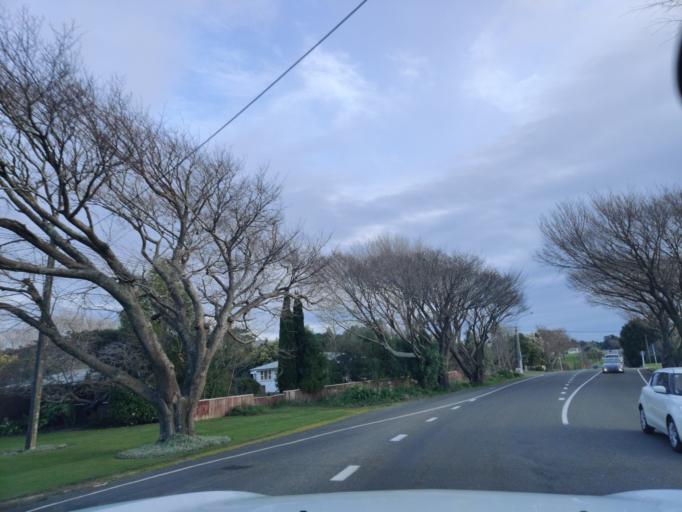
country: NZ
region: Manawatu-Wanganui
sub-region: Horowhenua District
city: Foxton
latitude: -40.5512
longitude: 175.4148
